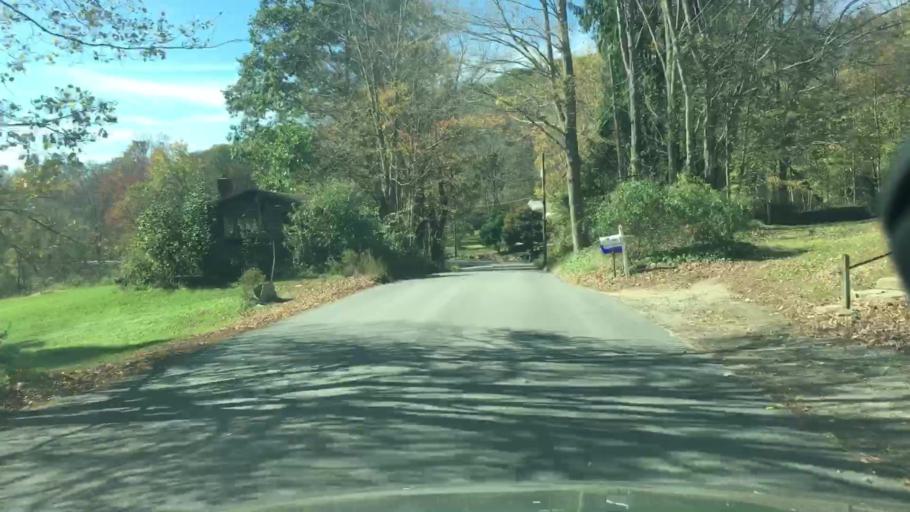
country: US
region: Connecticut
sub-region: Tolland County
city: Stafford
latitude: 41.9904
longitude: -72.2865
